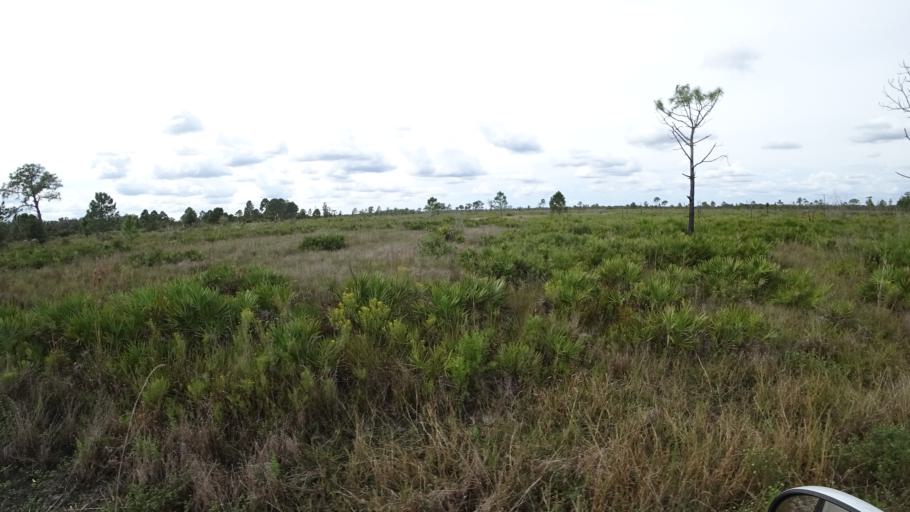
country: US
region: Florida
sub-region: Hillsborough County
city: Wimauma
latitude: 27.5538
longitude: -82.1332
